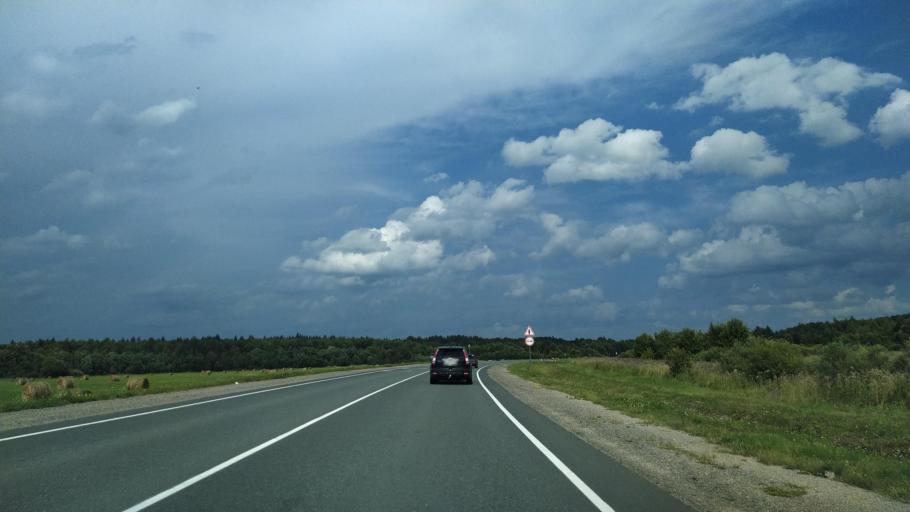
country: RU
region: Pskov
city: Porkhov
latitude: 57.8553
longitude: 29.5543
